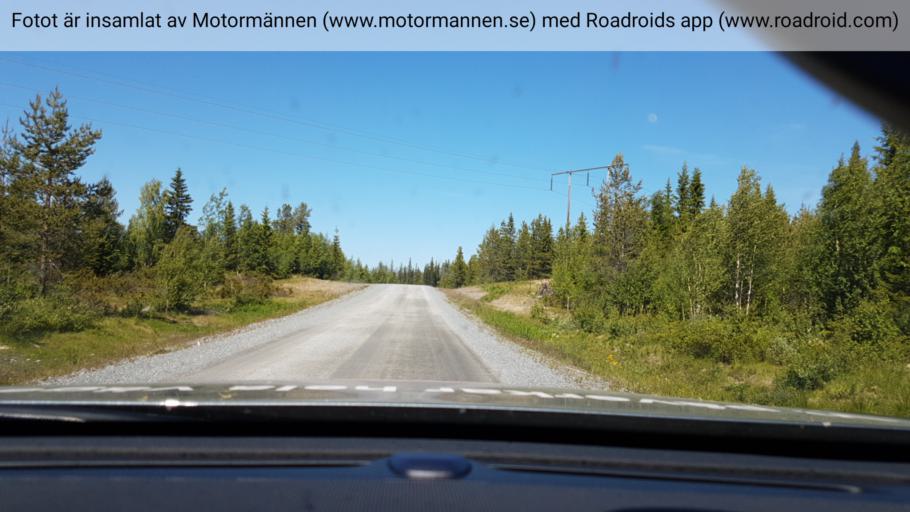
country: SE
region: Vaesterbotten
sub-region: Vilhelmina Kommun
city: Sjoberg
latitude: 64.6781
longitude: 15.7550
